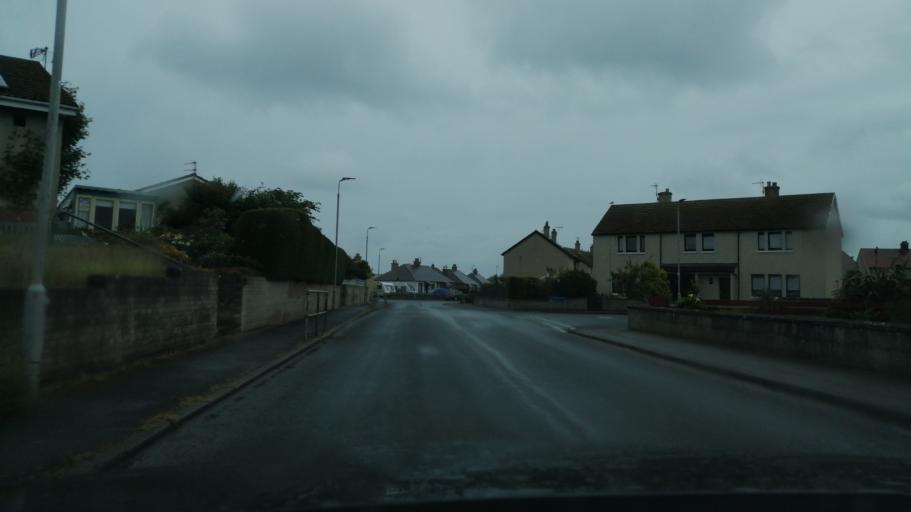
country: GB
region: Scotland
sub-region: Aberdeenshire
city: Portsoy
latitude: 57.6812
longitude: -2.6991
